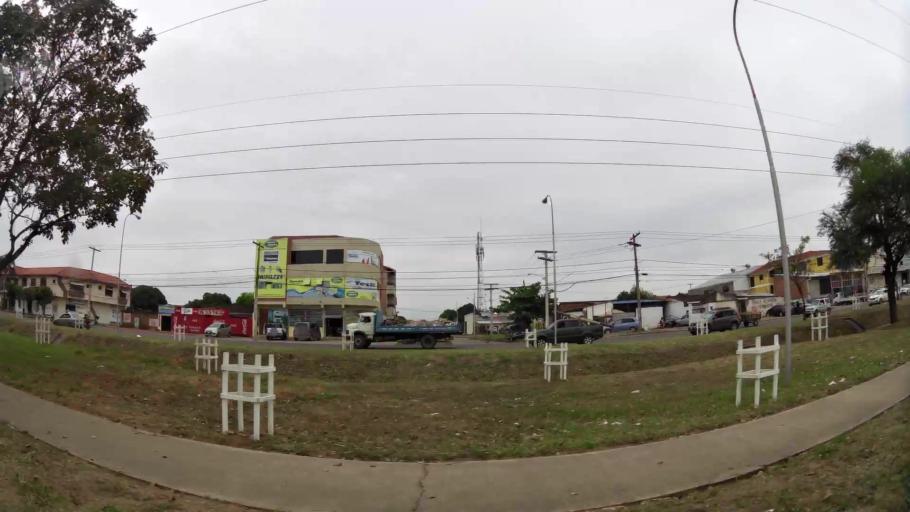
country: BO
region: Santa Cruz
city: Santa Cruz de la Sierra
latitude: -17.7630
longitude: -63.1497
